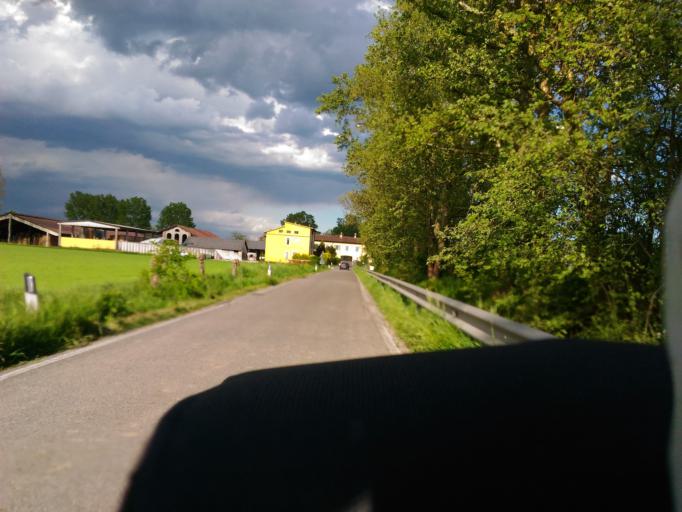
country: IT
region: Lombardy
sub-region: Citta metropolitana di Milano
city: Triginto
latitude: 45.4015
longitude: 9.3122
